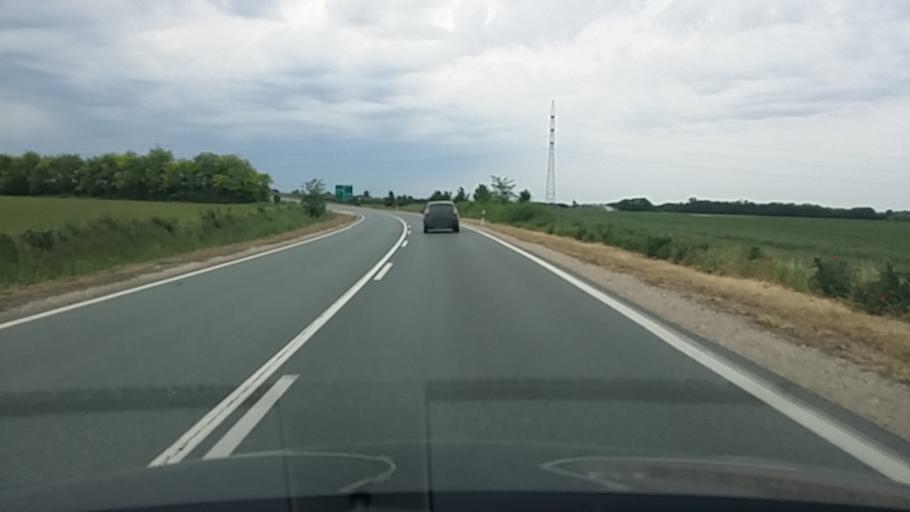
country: HU
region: Fejer
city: dunaujvaros
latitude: 46.9910
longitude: 18.8939
